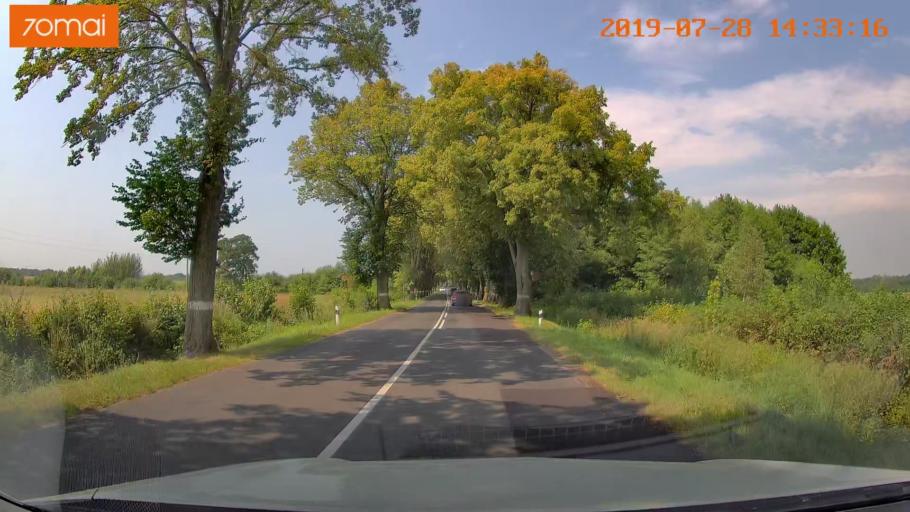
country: RU
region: Kaliningrad
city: Primorsk
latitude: 54.8185
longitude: 20.0333
